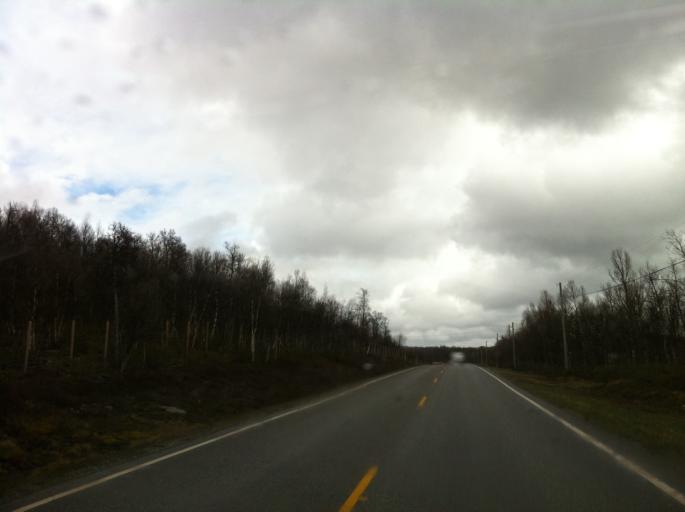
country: NO
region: Sor-Trondelag
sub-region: Tydal
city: Aas
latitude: 62.6410
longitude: 11.8893
